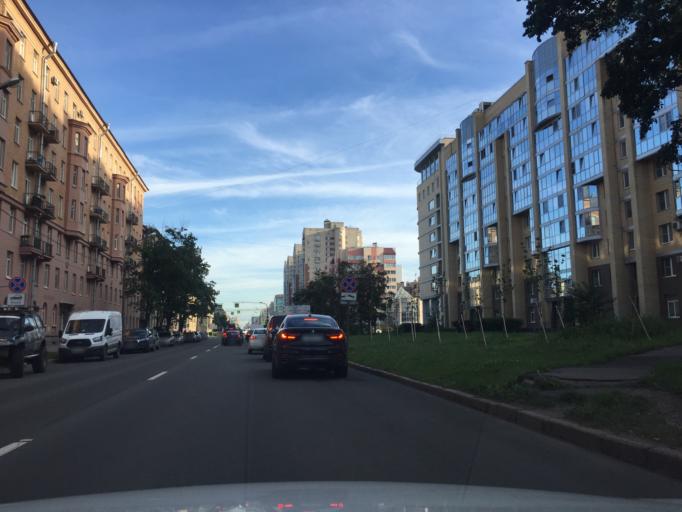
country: RU
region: St.-Petersburg
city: Admiralteisky
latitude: 59.8772
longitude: 30.3133
